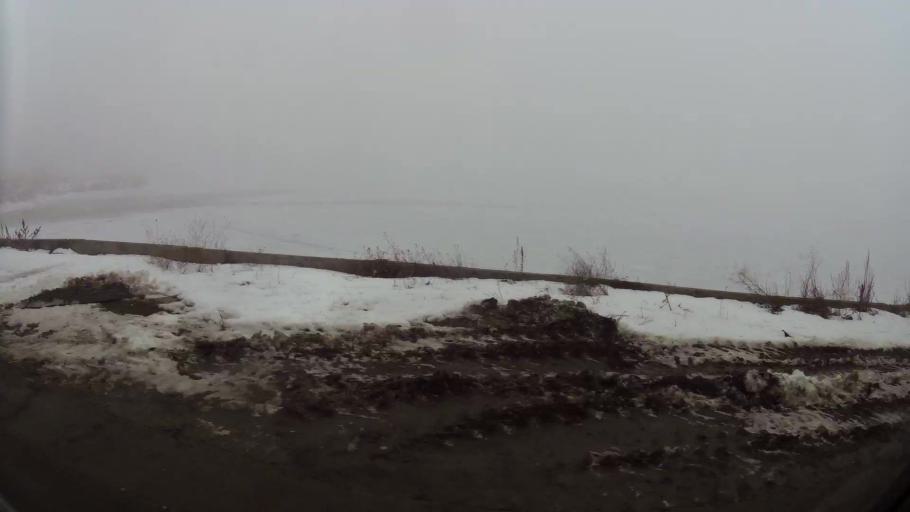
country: RO
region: Ilfov
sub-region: Comuna Chiajna
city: Rosu
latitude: 44.4489
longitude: 26.0214
